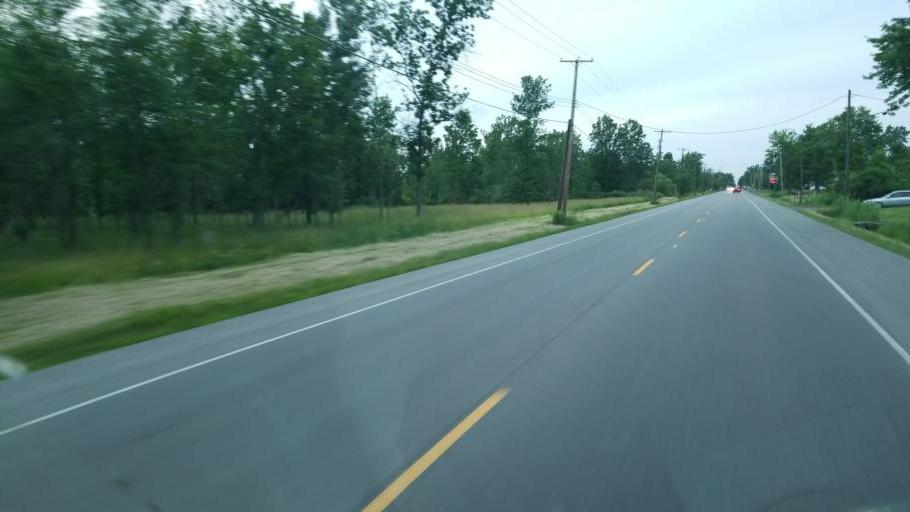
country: US
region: New York
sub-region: Niagara County
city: Rapids
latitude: 43.0531
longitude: -78.6969
